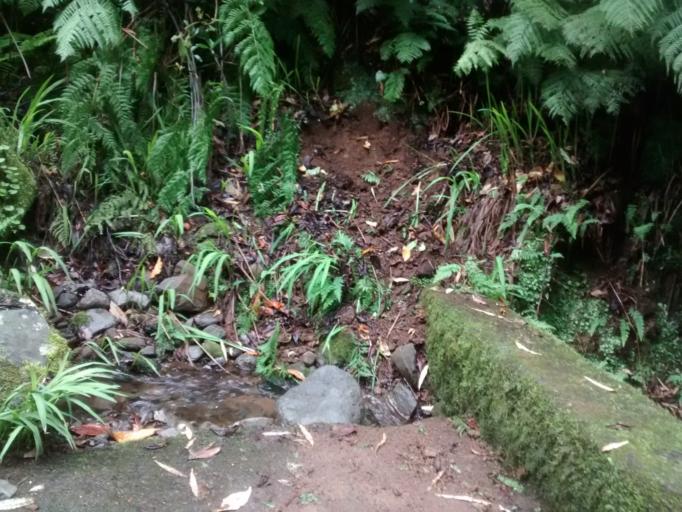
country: PT
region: Madeira
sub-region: Santana
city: Santana
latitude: 32.8067
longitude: -16.9396
